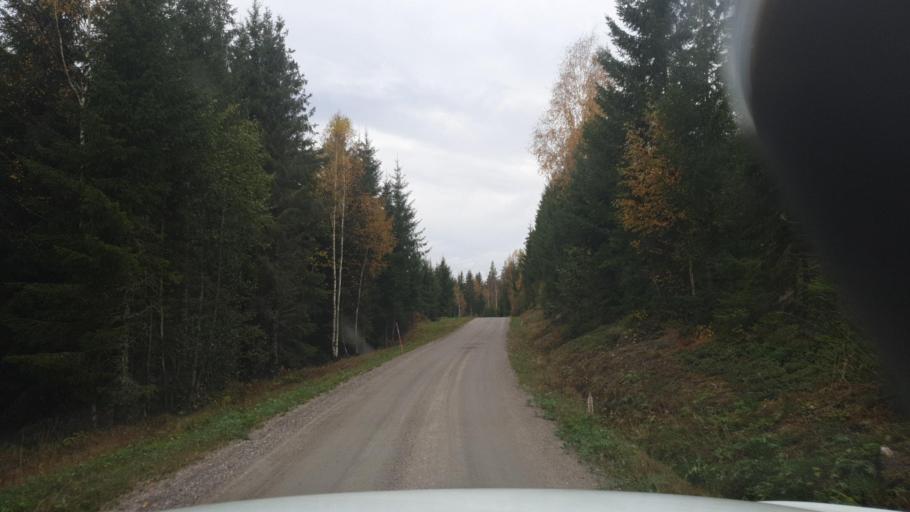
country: SE
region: Vaermland
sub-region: Arvika Kommun
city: Arvika
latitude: 59.8356
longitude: 12.7663
